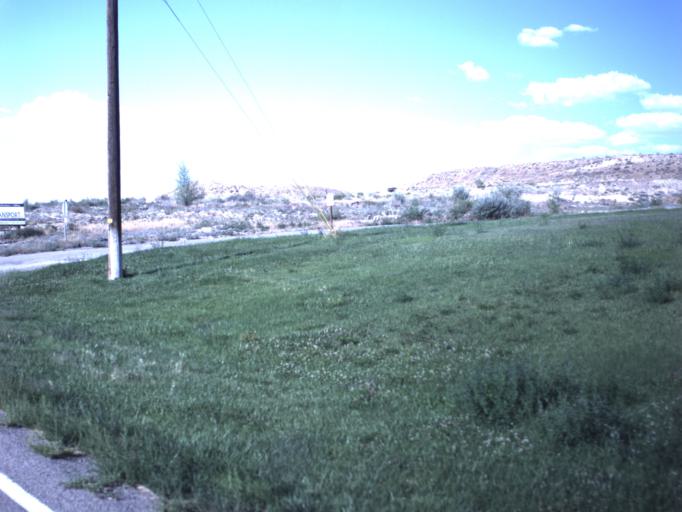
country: US
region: Utah
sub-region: Emery County
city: Huntington
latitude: 39.3634
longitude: -110.8520
